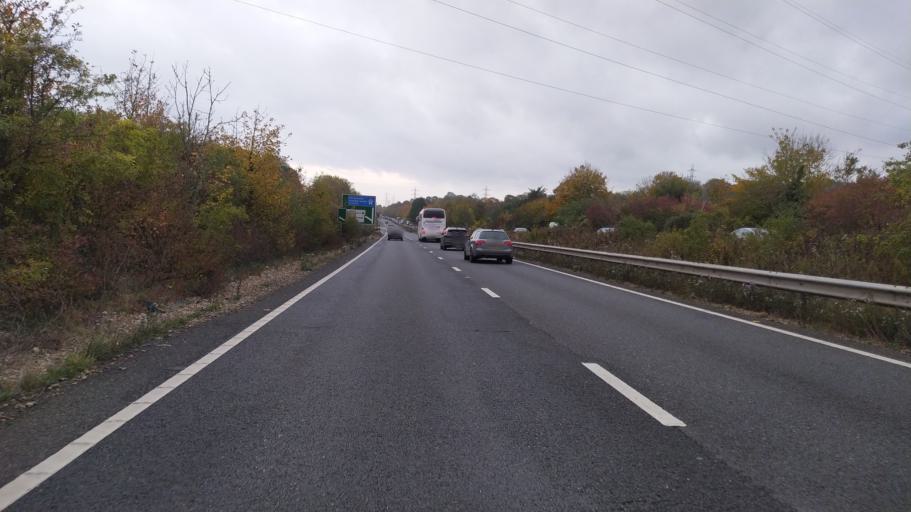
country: GB
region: England
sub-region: Hampshire
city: Cowplain
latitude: 50.9252
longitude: -0.9973
